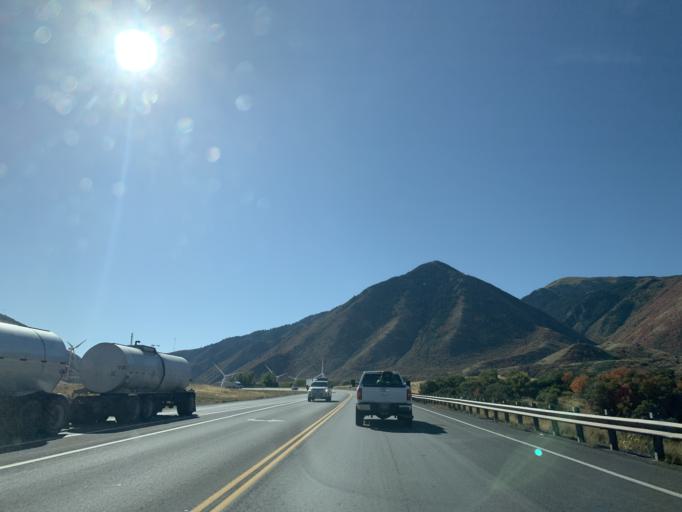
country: US
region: Utah
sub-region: Utah County
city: Mapleton
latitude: 40.0863
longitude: -111.5947
